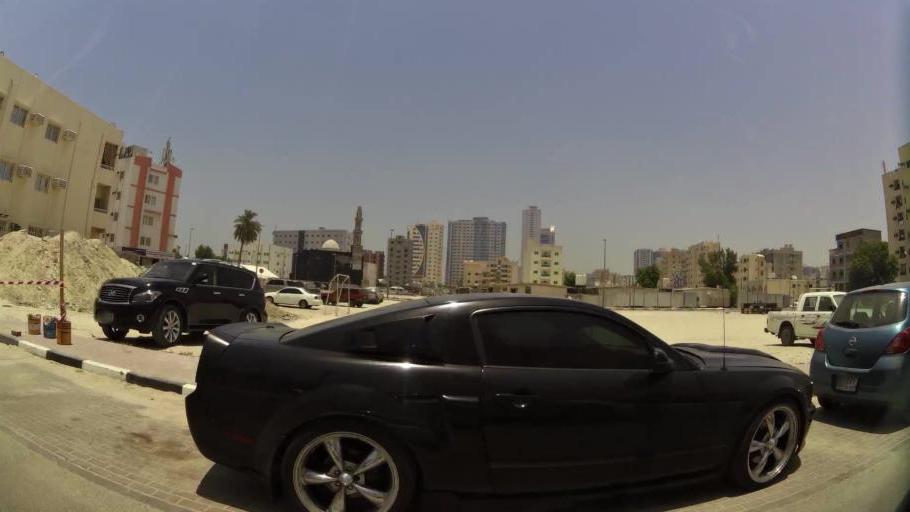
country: AE
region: Ajman
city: Ajman
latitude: 25.4103
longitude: 55.4363
